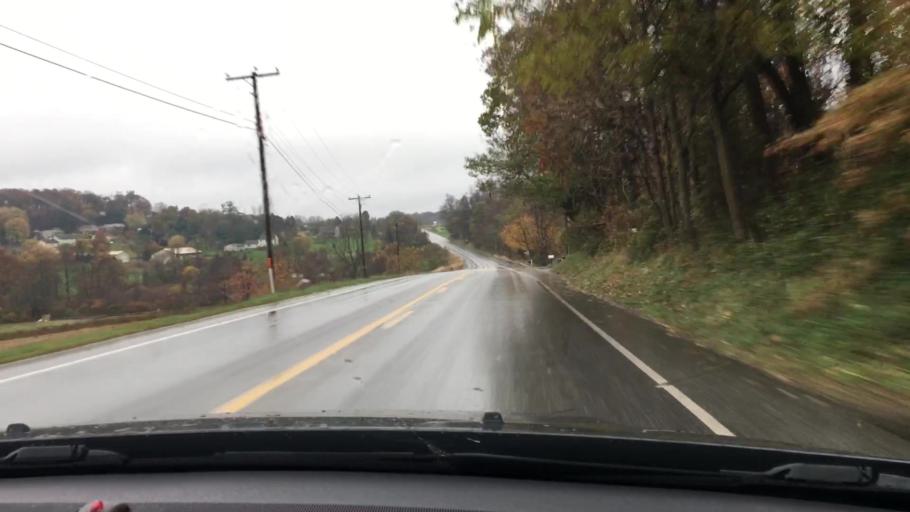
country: US
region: Pennsylvania
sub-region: Lancaster County
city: Conestoga
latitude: 39.8505
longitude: -76.2959
